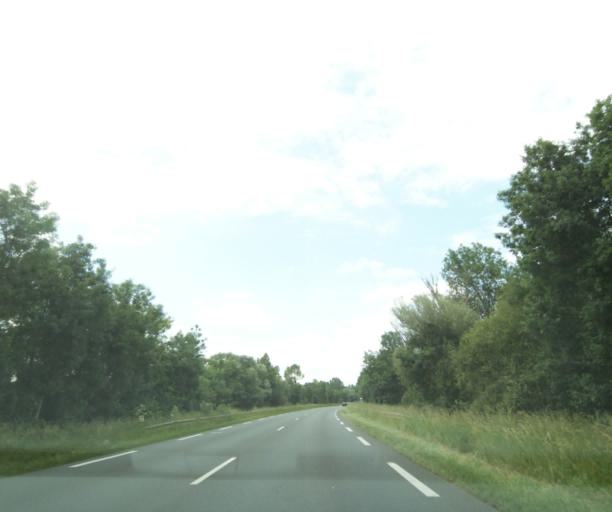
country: FR
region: Pays de la Loire
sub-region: Departement de Maine-et-Loire
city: Montreuil-Bellay
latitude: 47.1267
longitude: -0.1664
